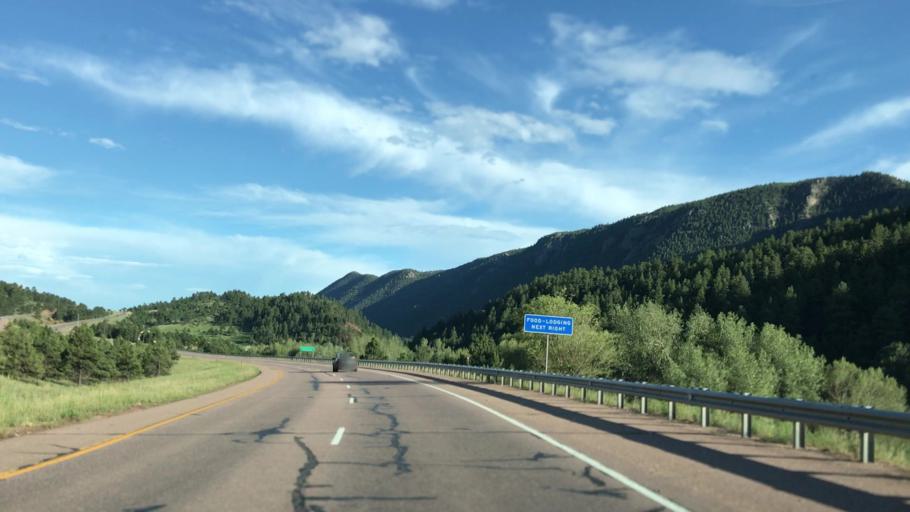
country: US
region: Colorado
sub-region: El Paso County
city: Cascade-Chipita Park
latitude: 38.9448
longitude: -105.0205
